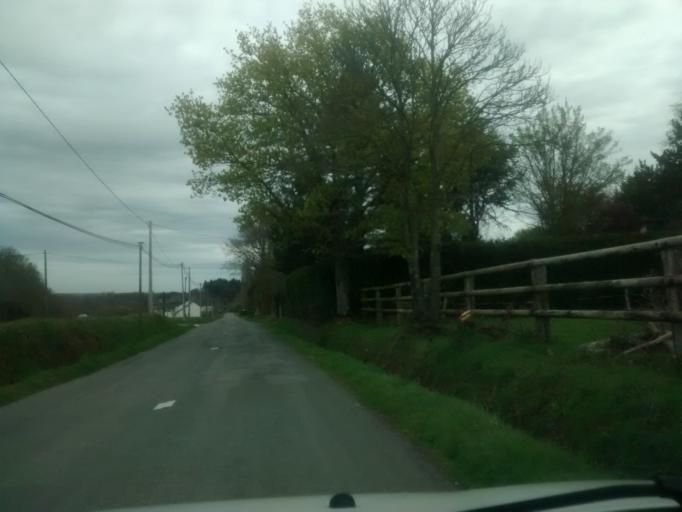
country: FR
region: Brittany
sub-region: Departement d'Ille-et-Vilaine
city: Saint-Sulpice-la-Foret
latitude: 48.2011
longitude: -1.5965
